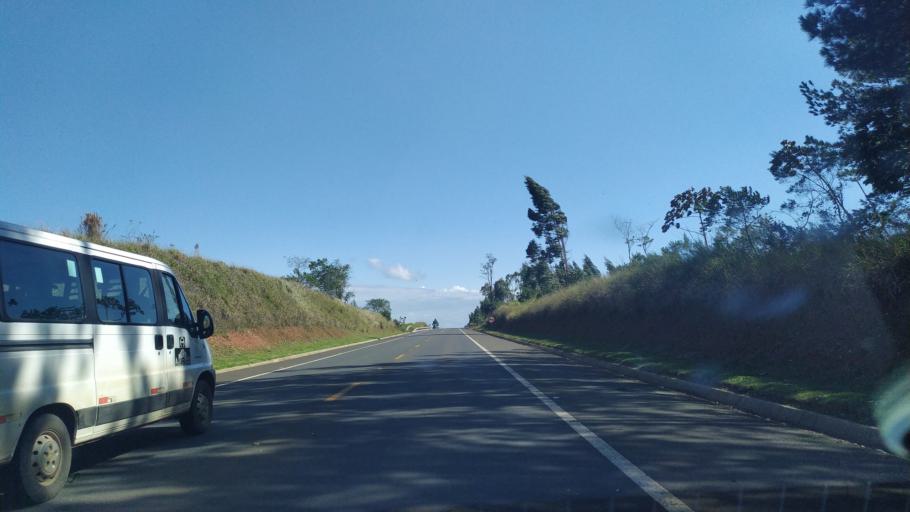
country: BR
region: Parana
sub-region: Ortigueira
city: Ortigueira
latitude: -24.2565
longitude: -50.7822
